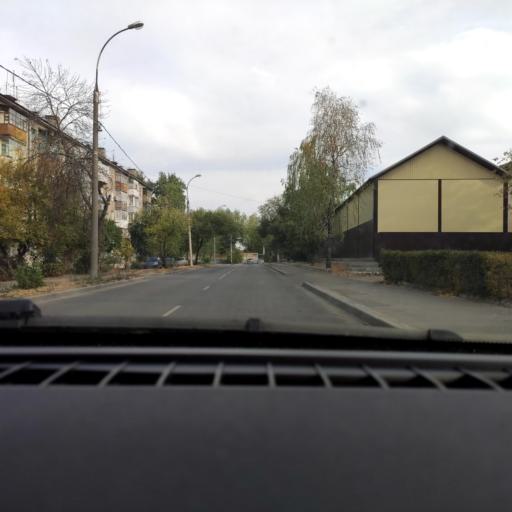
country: RU
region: Voronezj
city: Voronezh
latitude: 51.6406
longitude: 39.2458
